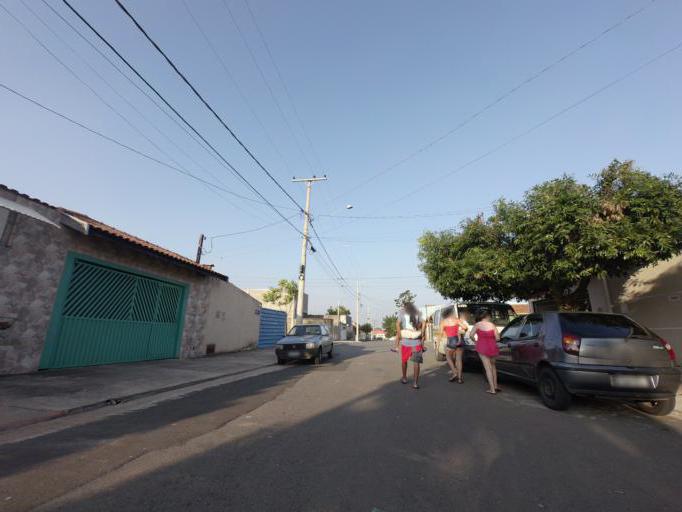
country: BR
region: Sao Paulo
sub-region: Piracicaba
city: Piracicaba
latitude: -22.7500
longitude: -47.6010
